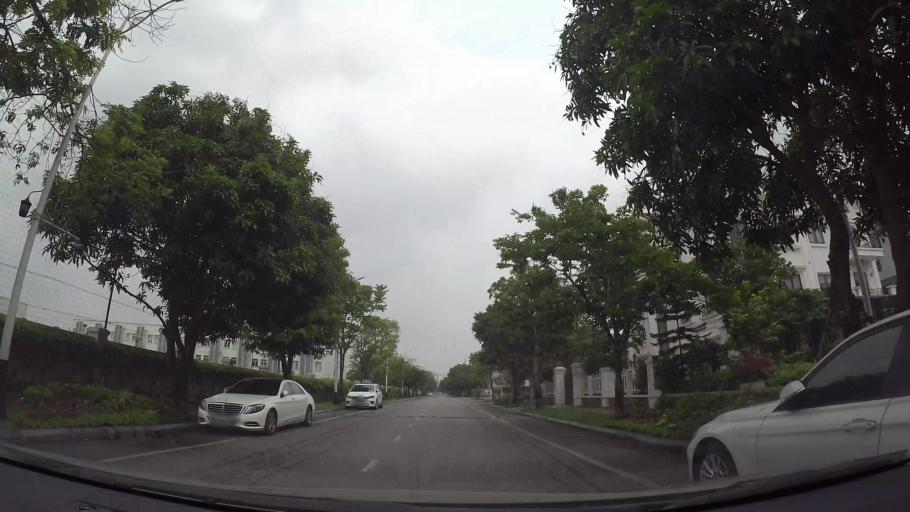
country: VN
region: Ha Noi
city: Trau Quy
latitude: 21.0435
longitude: 105.9201
